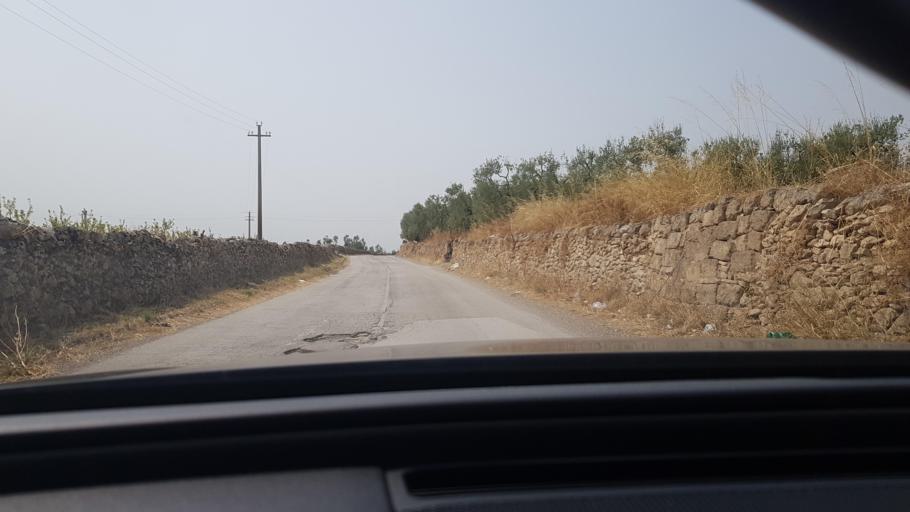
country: IT
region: Apulia
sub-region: Provincia di Barletta - Andria - Trani
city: Andria
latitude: 41.2206
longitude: 16.2638
